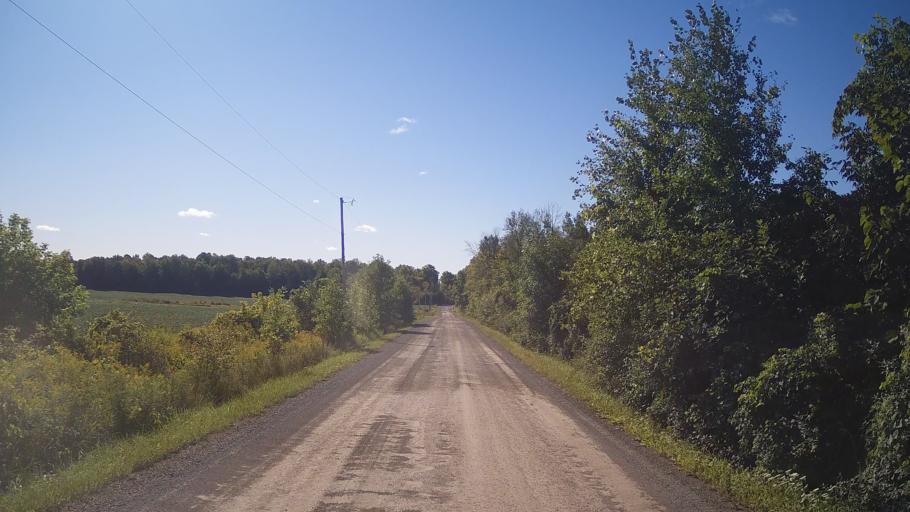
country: CA
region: Ontario
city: Prescott
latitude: 44.9717
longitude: -75.5679
